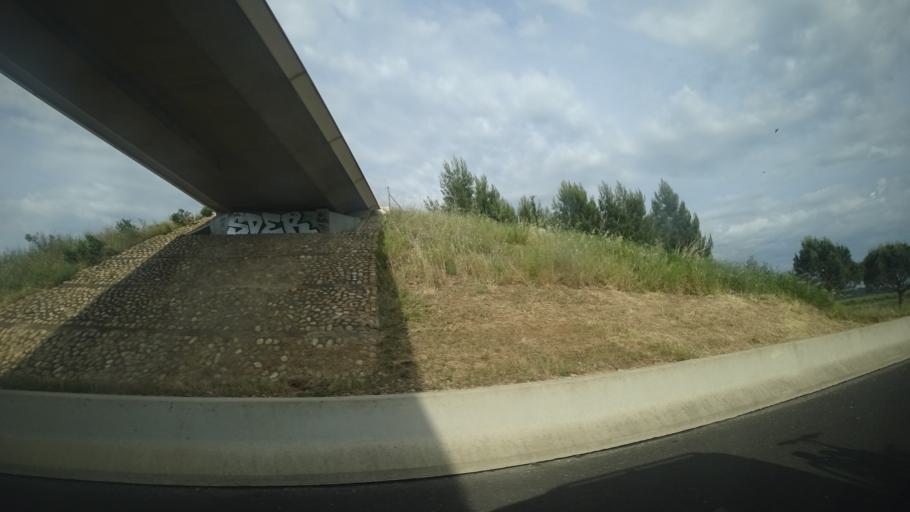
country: FR
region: Languedoc-Roussillon
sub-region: Departement de l'Herault
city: Aspiran
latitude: 43.5947
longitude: 3.4651
